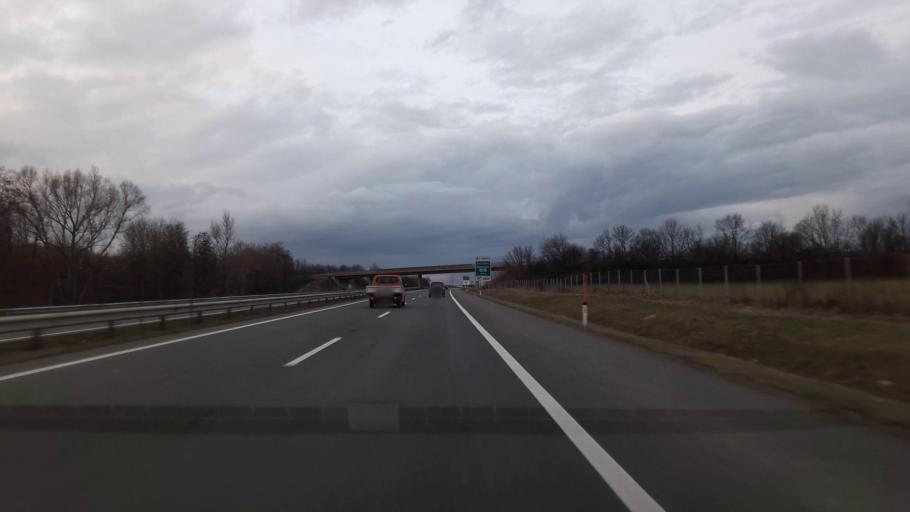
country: AT
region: Burgenland
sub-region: Eisenstadt-Umgebung
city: Steinbrunn
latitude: 47.8553
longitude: 16.4249
